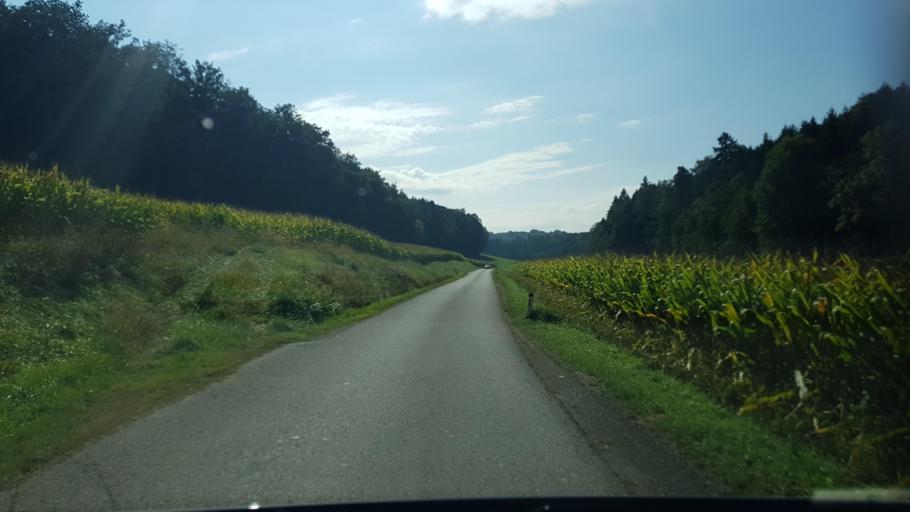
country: AT
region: Styria
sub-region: Politischer Bezirk Deutschlandsberg
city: Wettmannstatten
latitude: 46.8181
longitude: 15.3769
